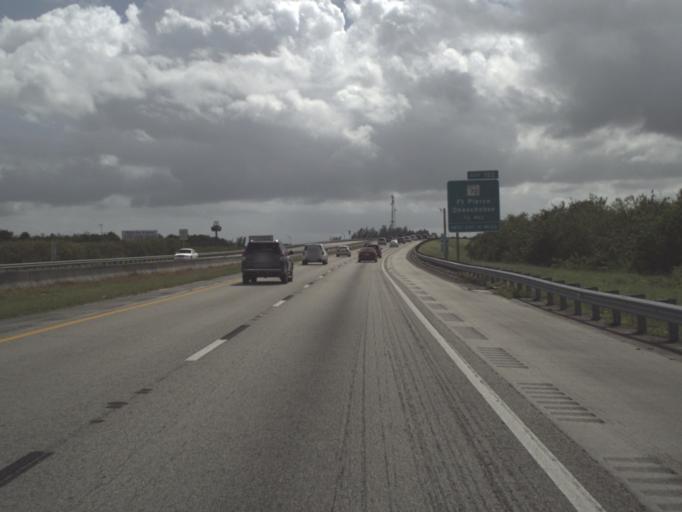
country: US
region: Florida
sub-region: Saint Lucie County
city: Fort Pierce South
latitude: 27.4167
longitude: -80.4048
